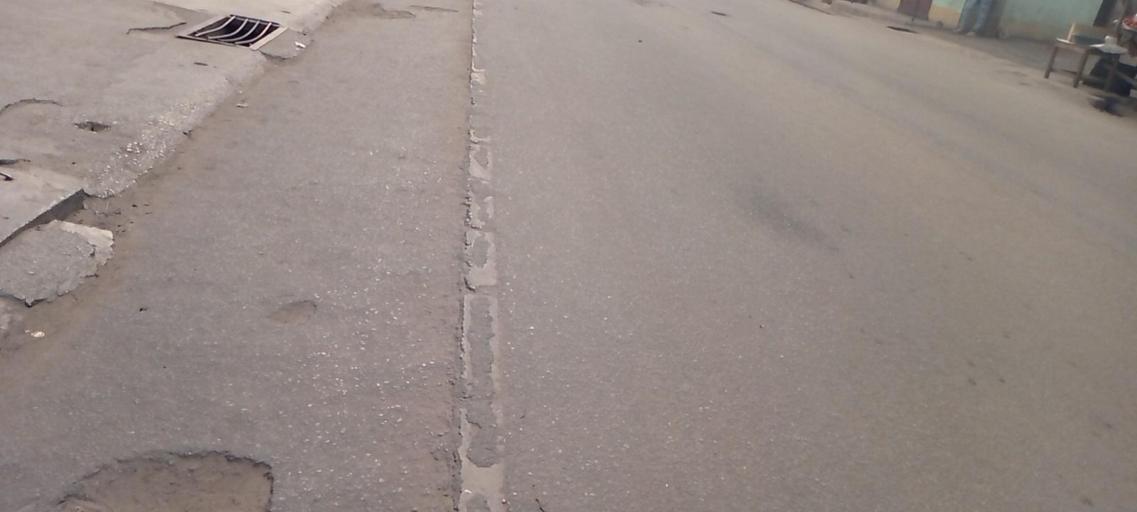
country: ZM
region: Lusaka
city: Lusaka
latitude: -15.4024
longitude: 28.3509
